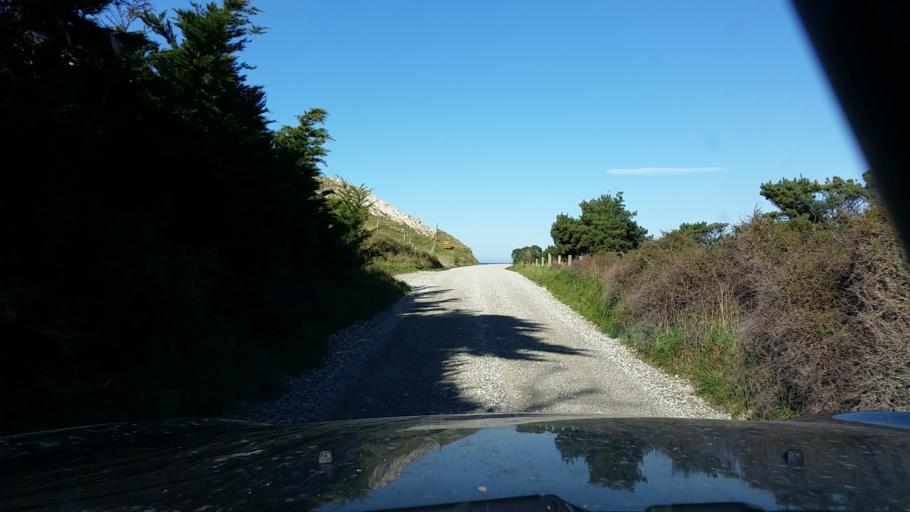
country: NZ
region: Marlborough
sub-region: Marlborough District
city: Blenheim
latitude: -41.8430
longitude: 174.1814
